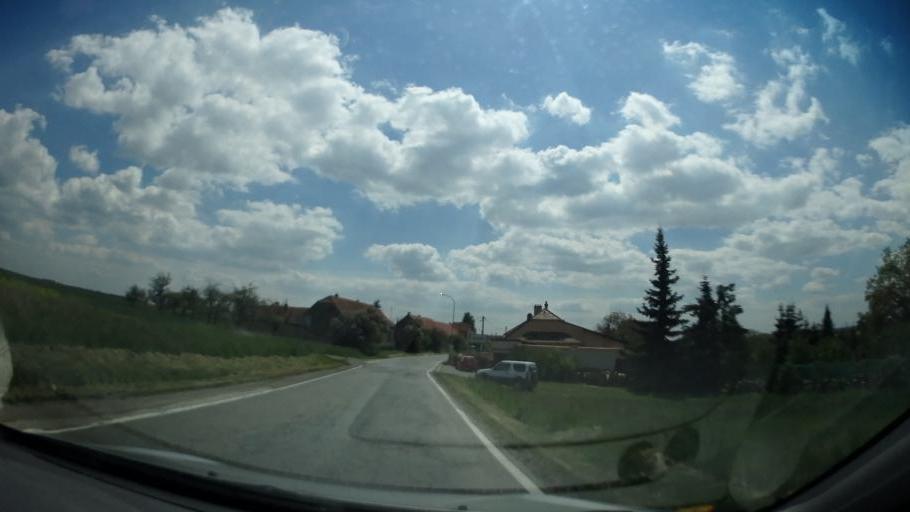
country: CZ
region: Vysocina
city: Hrotovice
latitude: 49.1360
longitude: 16.0801
